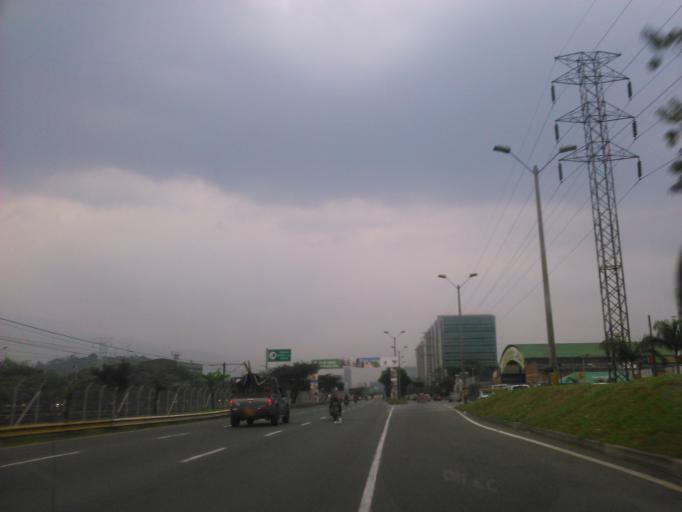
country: CO
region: Antioquia
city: Medellin
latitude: 6.2230
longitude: -75.5764
